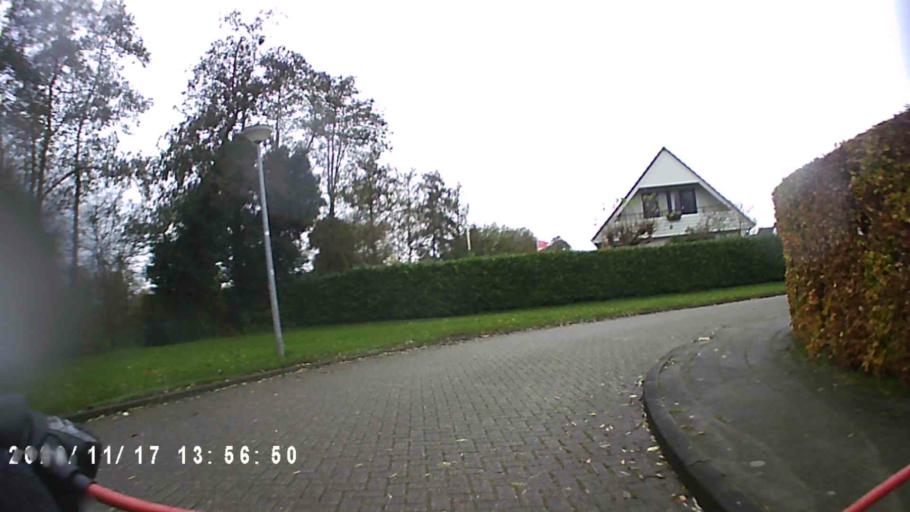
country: NL
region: Groningen
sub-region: Gemeente Zuidhorn
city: Grijpskerk
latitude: 53.2217
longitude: 6.3484
